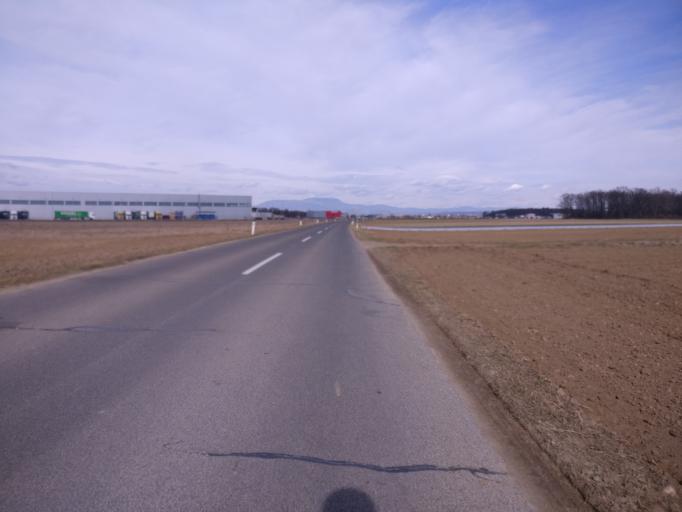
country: AT
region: Styria
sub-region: Politischer Bezirk Graz-Umgebung
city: Zettling
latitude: 46.9589
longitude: 15.4456
